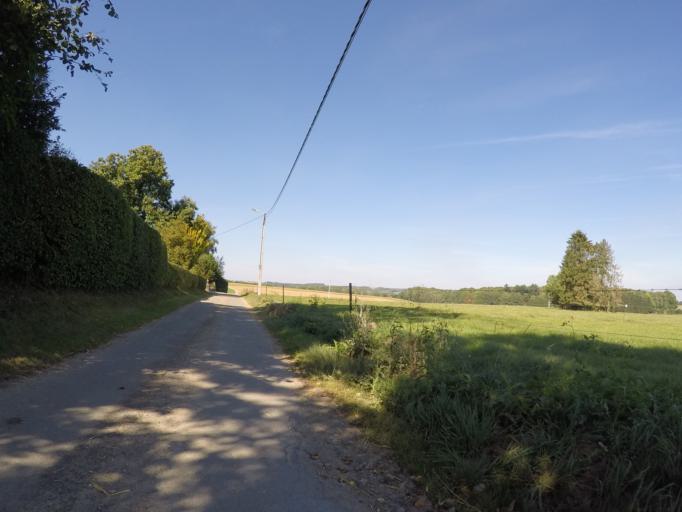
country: BE
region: Wallonia
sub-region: Province de Namur
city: Assesse
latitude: 50.3024
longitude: 5.0268
